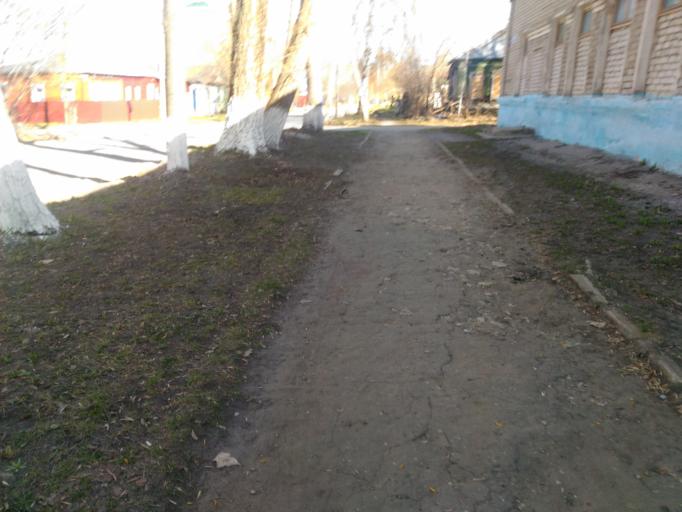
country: RU
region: Ulyanovsk
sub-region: Ulyanovskiy Rayon
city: Ulyanovsk
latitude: 54.3465
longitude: 48.3811
